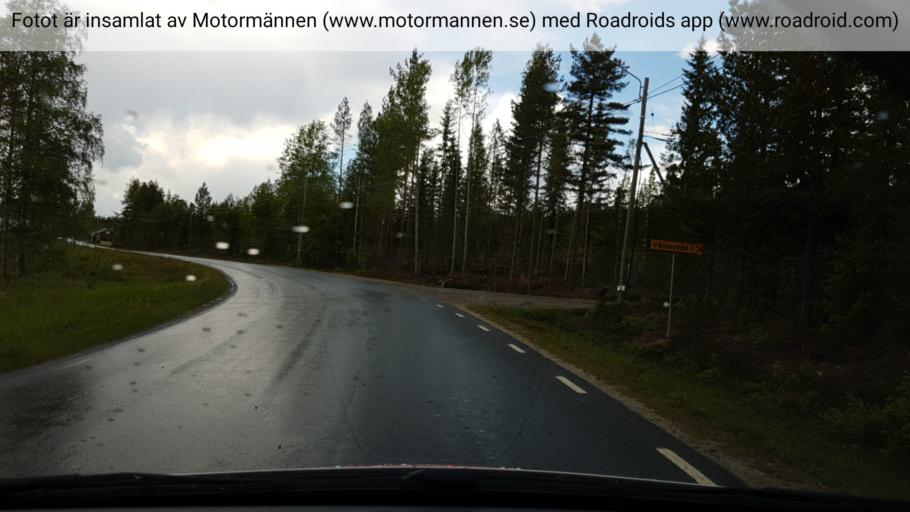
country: SE
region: Vaesterbotten
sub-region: Umea Kommun
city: Roback
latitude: 63.9941
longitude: 20.1107
